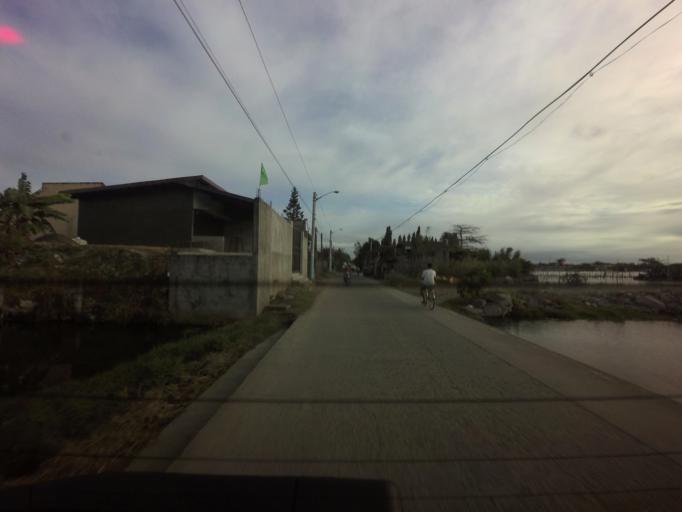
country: PH
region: Central Luzon
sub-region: Province of Bulacan
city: Obando
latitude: 14.7283
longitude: 120.9298
